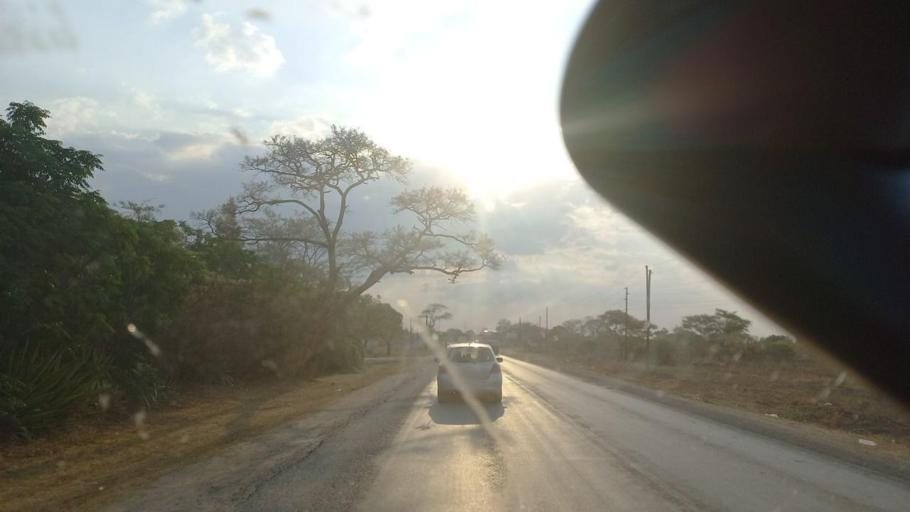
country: ZM
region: Lusaka
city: Lusaka
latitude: -15.3679
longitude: 28.4140
